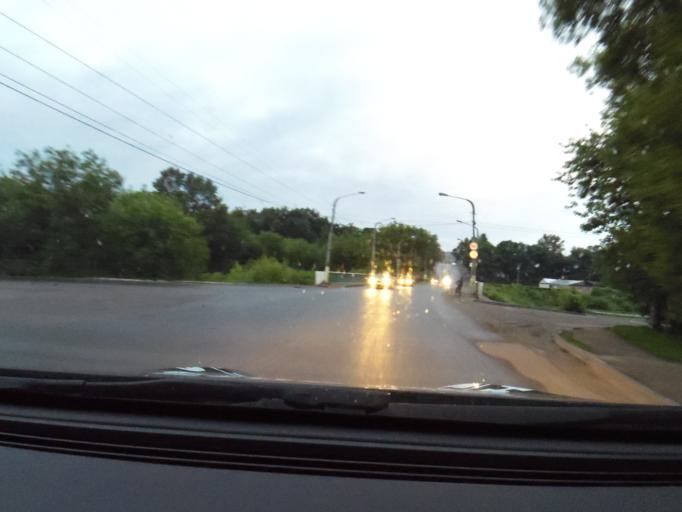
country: RU
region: Vladimir
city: Aleksandrov
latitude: 56.3981
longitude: 38.7374
